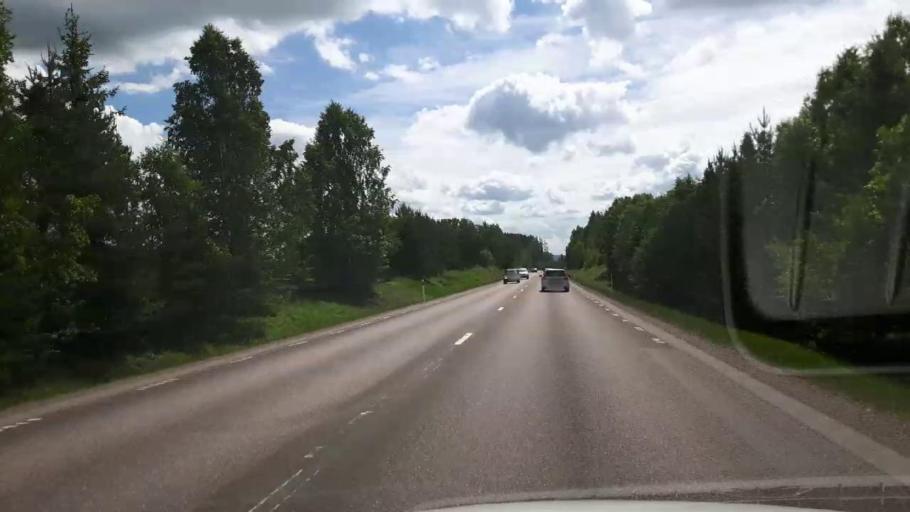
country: SE
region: Dalarna
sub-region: Saters Kommun
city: Saeter
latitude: 60.4605
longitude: 15.8019
